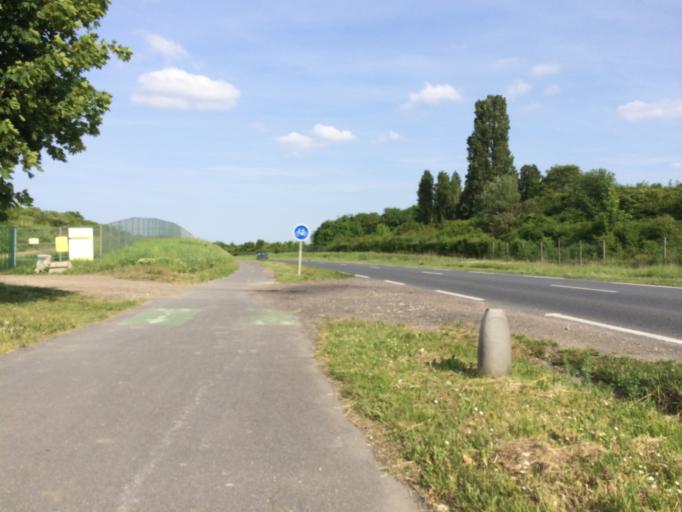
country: FR
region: Ile-de-France
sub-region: Departement de l'Essonne
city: Morangis
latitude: 48.7136
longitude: 2.3404
